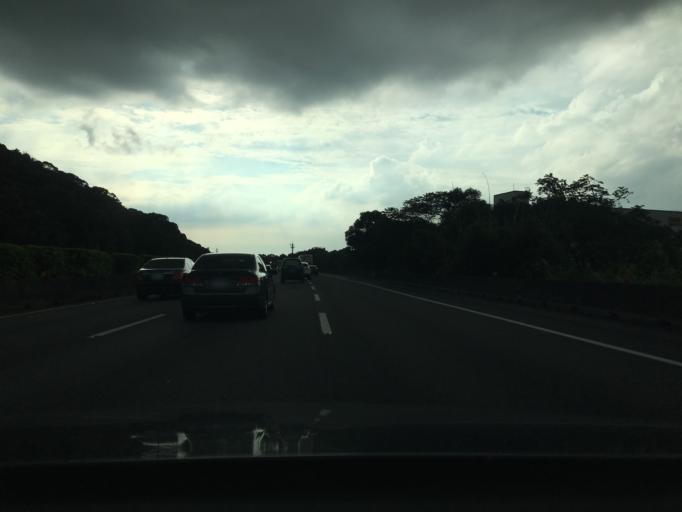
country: TW
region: Taiwan
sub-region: Hsinchu
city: Zhubei
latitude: 24.8846
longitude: 121.0812
